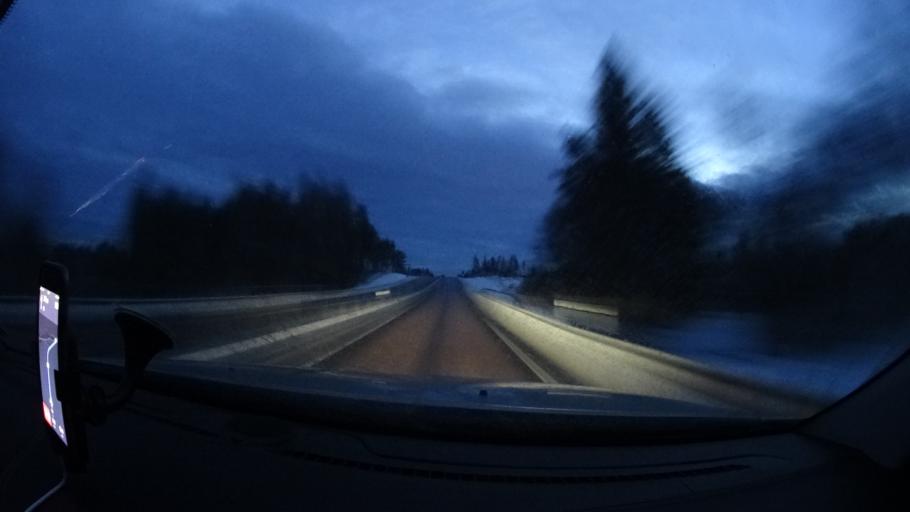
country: SE
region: Gaevleborg
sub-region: Hudiksvalls Kommun
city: Hudiksvall
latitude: 61.8210
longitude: 17.1908
